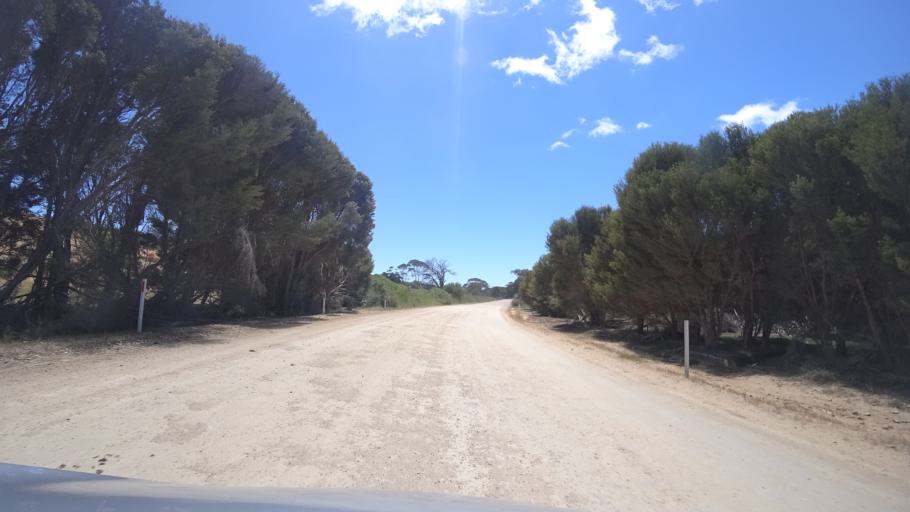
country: AU
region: South Australia
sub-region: Yankalilla
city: Normanville
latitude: -35.7948
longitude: 138.0637
